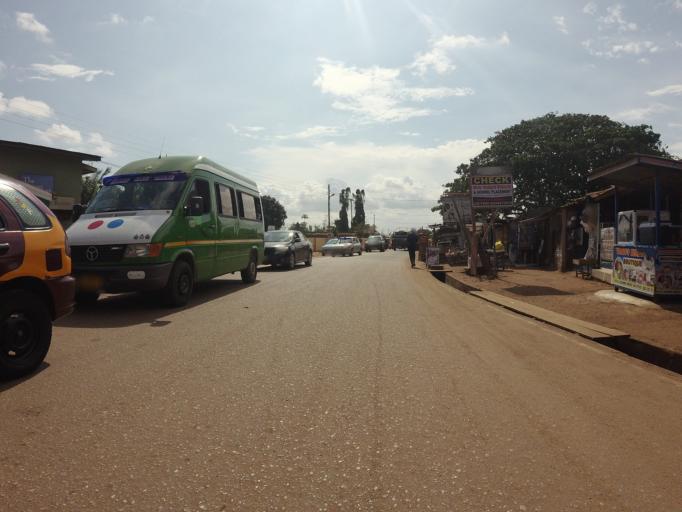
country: GH
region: Greater Accra
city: Medina Estates
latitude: 5.6785
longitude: -0.1741
